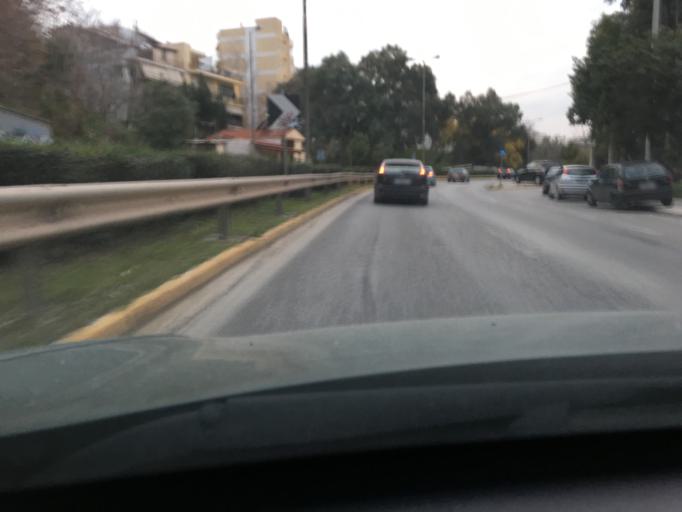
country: GR
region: Attica
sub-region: Nomarchia Athinas
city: Nea Ionia
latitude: 38.0385
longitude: 23.7550
